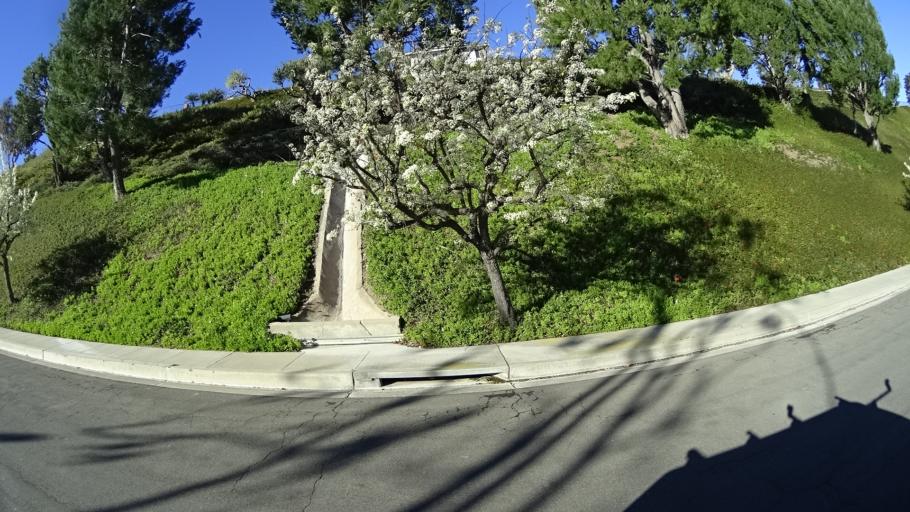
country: US
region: California
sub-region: Orange County
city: Villa Park
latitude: 33.8392
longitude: -117.8184
